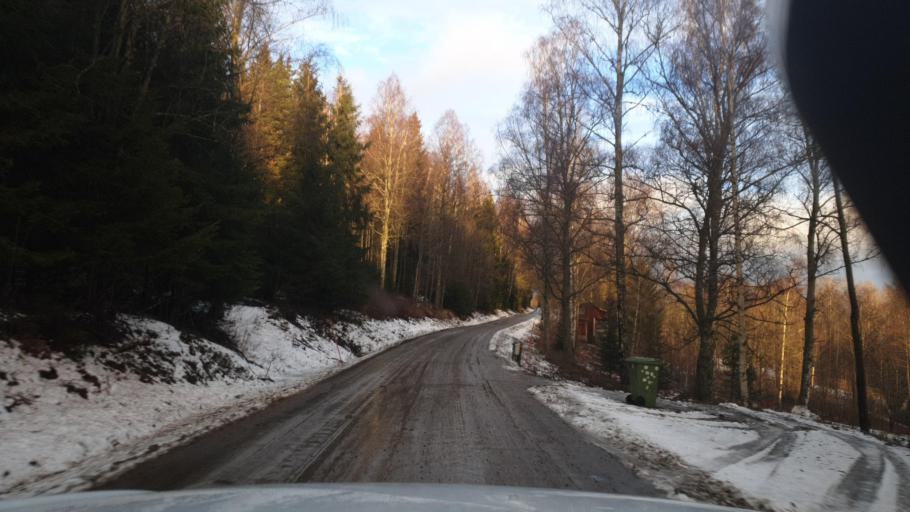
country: SE
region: Vaermland
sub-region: Eda Kommun
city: Amotfors
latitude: 59.7375
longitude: 12.2782
